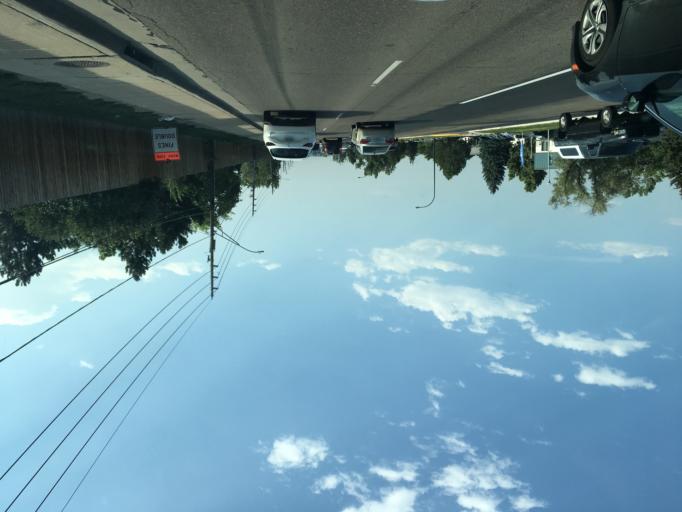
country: US
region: Colorado
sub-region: Adams County
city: Westminster
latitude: 39.8475
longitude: -105.0533
